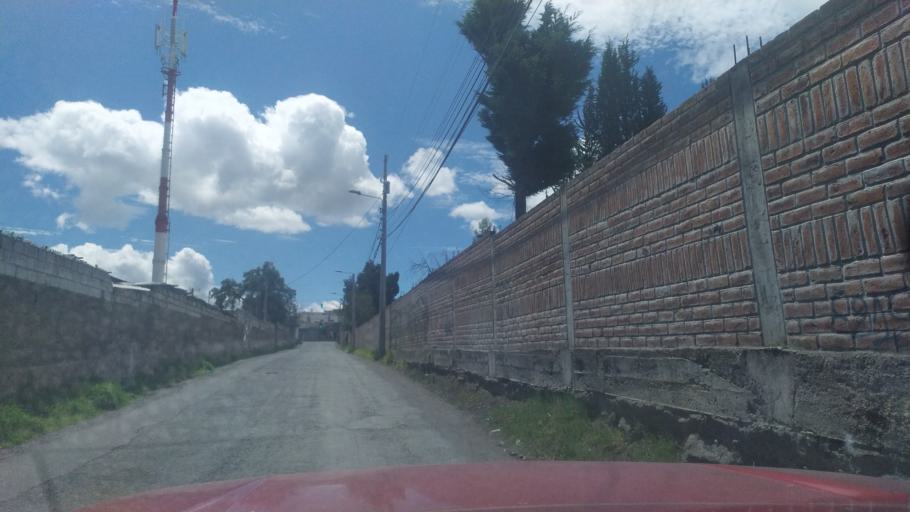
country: EC
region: Chimborazo
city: Riobamba
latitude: -1.6710
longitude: -78.6663
